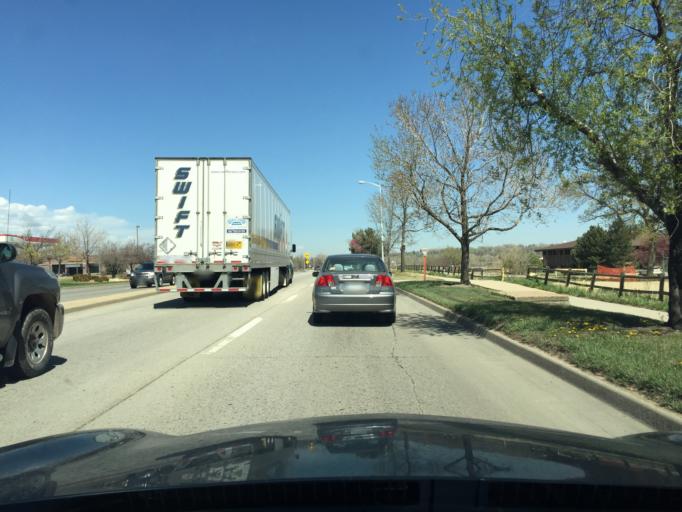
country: US
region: Colorado
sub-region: Boulder County
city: Longmont
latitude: 40.1532
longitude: -105.1305
